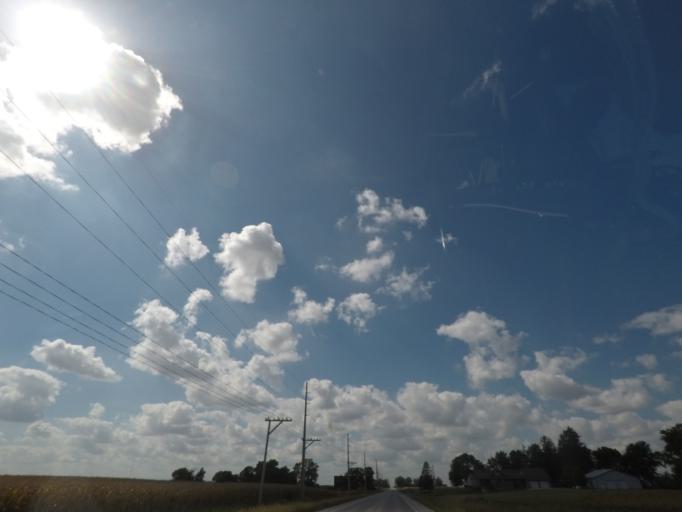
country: US
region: Iowa
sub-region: Story County
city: Nevada
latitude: 42.0231
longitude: -93.5362
